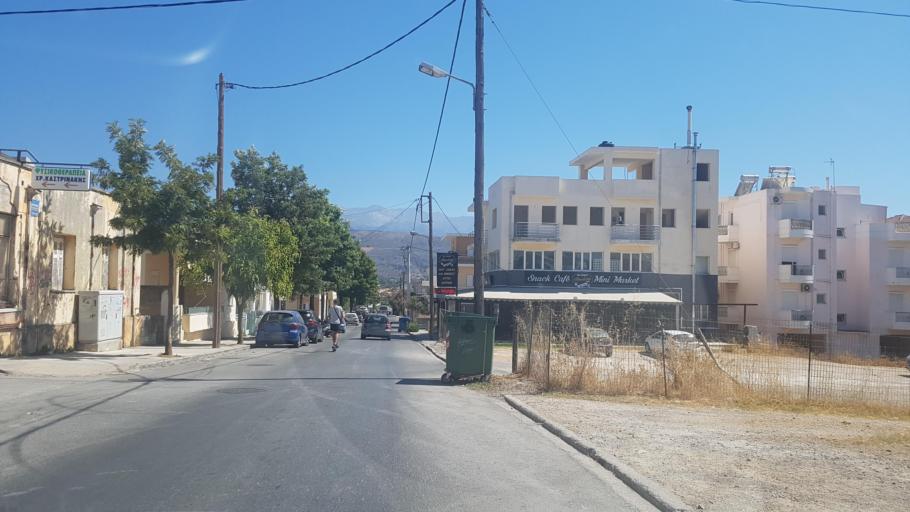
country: GR
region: Crete
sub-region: Nomos Chanias
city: Chania
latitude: 35.5070
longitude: 24.0176
